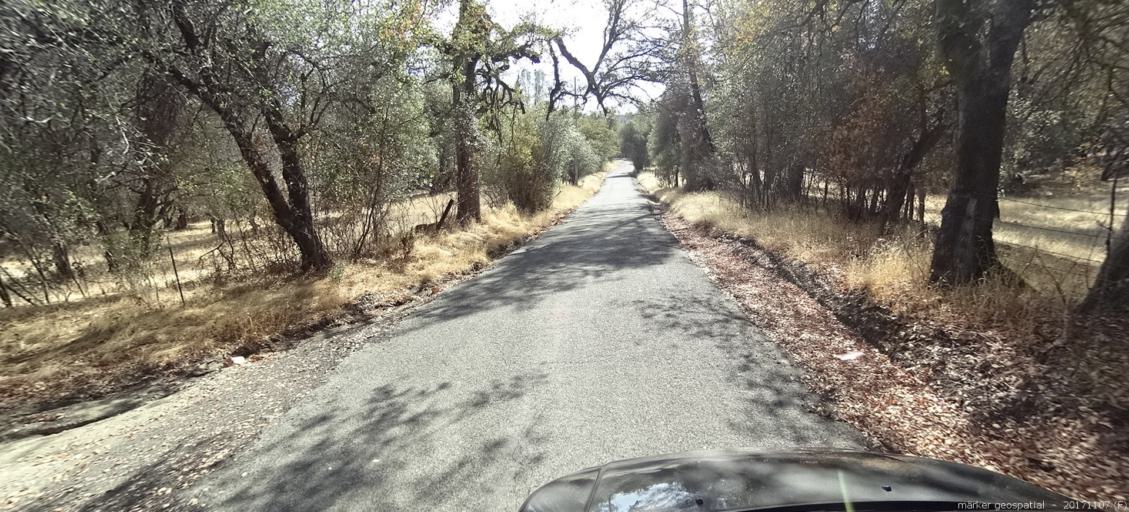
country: US
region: California
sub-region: Shasta County
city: Shasta
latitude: 40.5254
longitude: -122.5557
